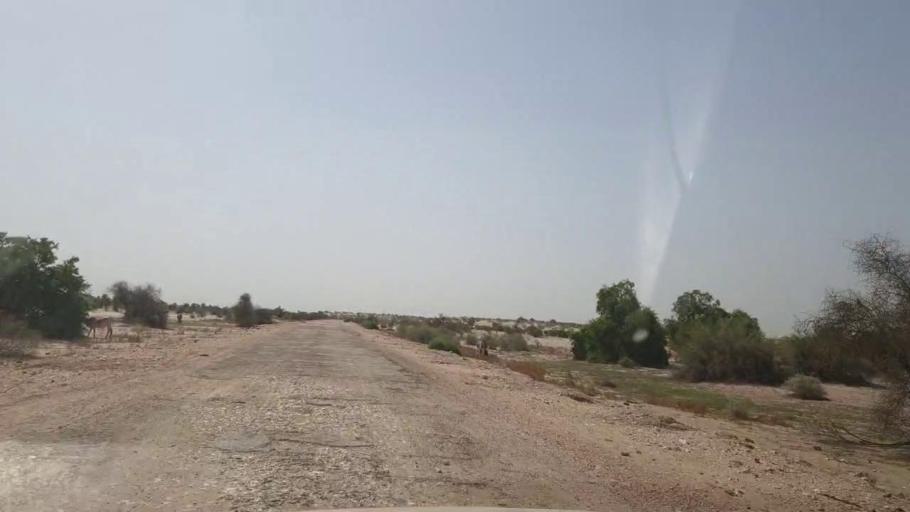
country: PK
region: Sindh
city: Rohri
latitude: 27.4405
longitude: 69.2420
